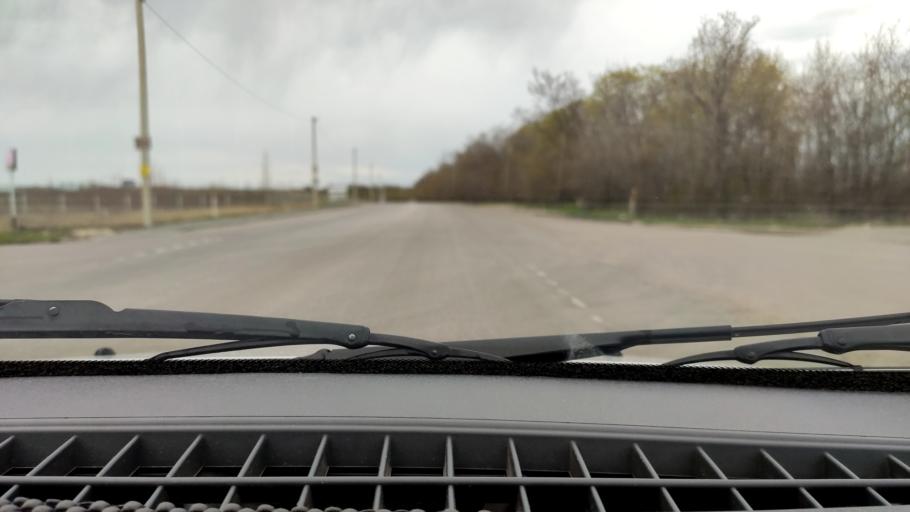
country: RU
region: Voronezj
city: Novaya Usman'
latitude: 51.6294
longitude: 39.3339
